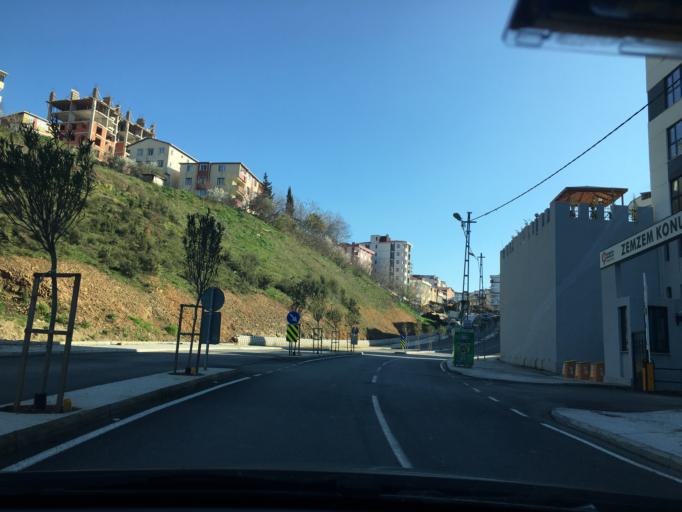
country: TR
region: Istanbul
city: Icmeler
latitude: 40.8713
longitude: 29.3019
